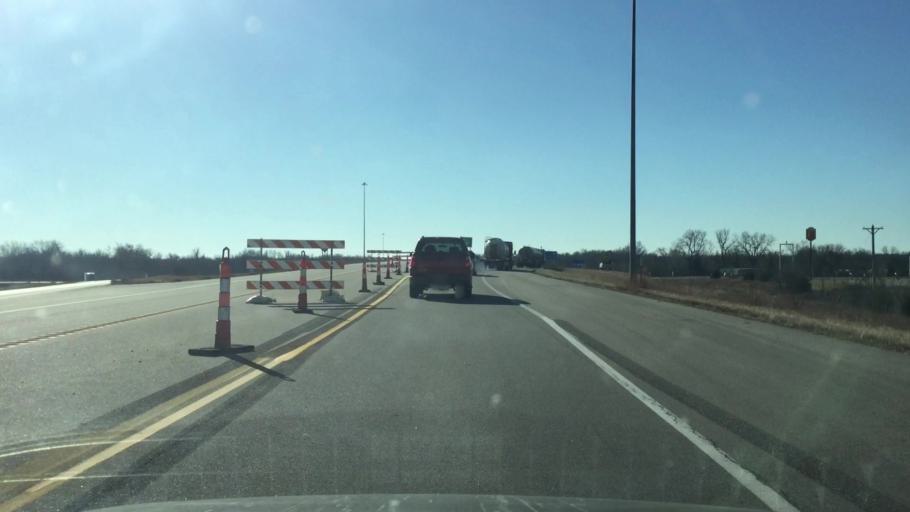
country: US
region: Kansas
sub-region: Allen County
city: Iola
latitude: 37.9254
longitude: -95.3797
